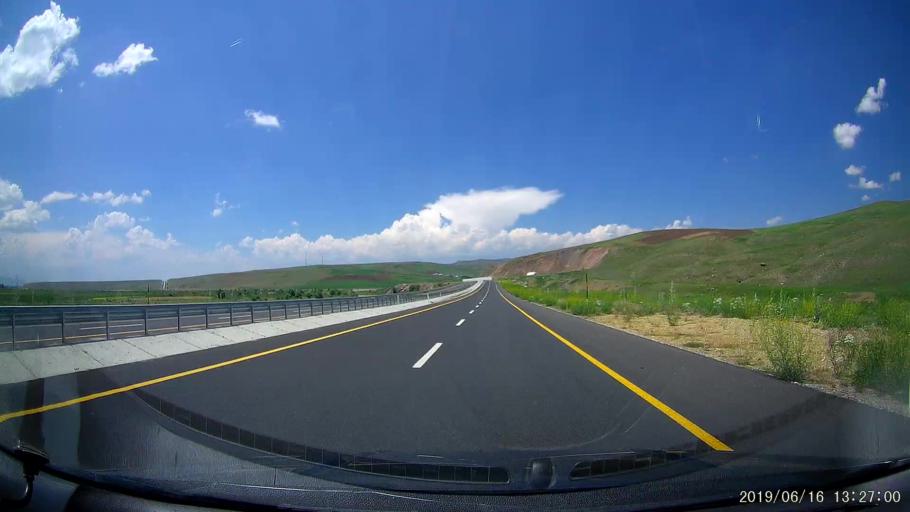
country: TR
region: Agri
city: Taslicay
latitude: 39.6651
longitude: 43.3174
